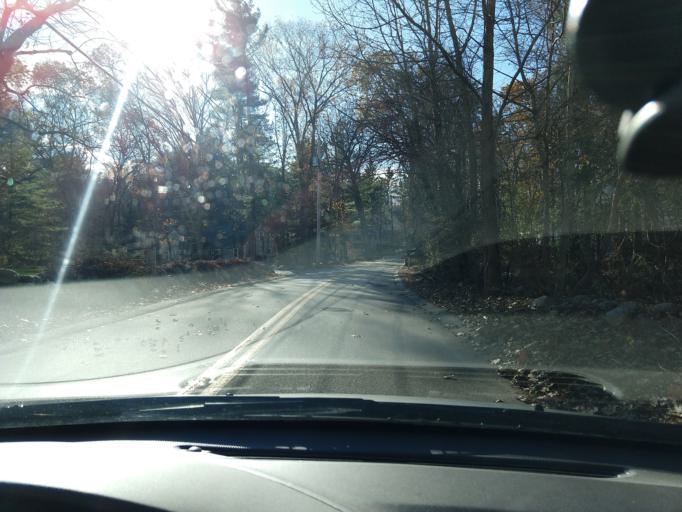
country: US
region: Massachusetts
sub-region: Middlesex County
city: Bedford
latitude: 42.5002
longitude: -71.2469
